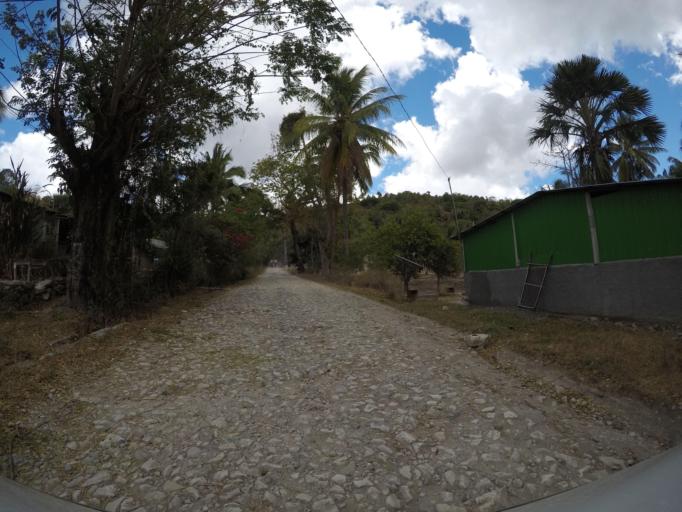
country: TL
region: Baucau
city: Baucau
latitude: -8.5082
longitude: 126.6787
